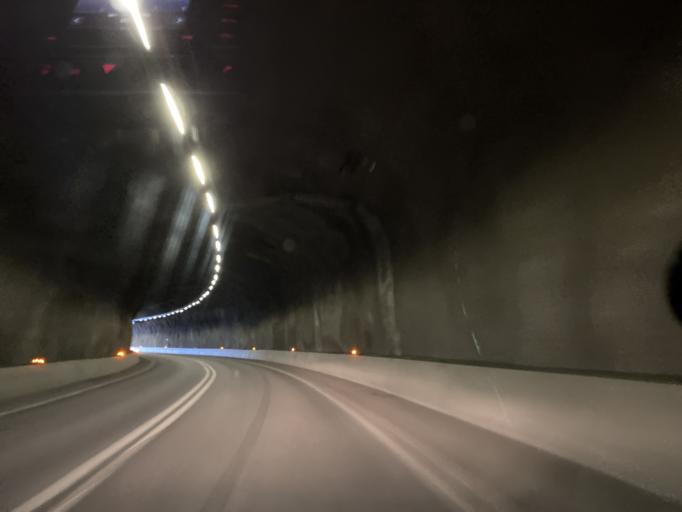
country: SE
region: Stockholm
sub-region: Nacka Kommun
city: Nacka
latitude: 59.3144
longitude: 18.1498
